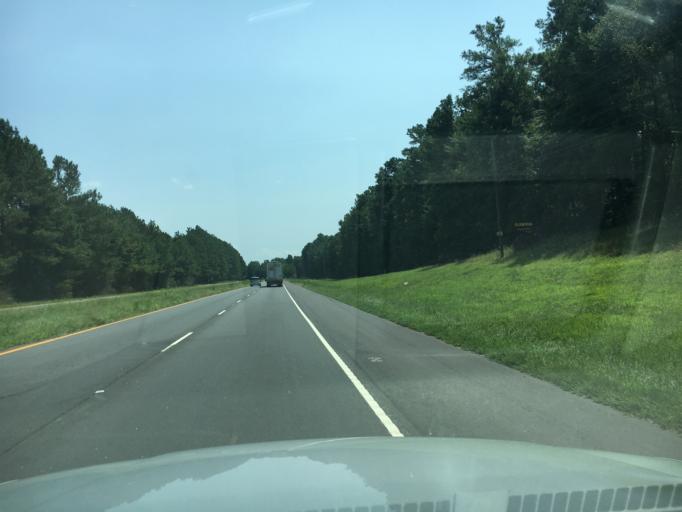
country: US
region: South Carolina
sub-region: Anderson County
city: Pendleton
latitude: 34.6543
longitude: -82.8108
